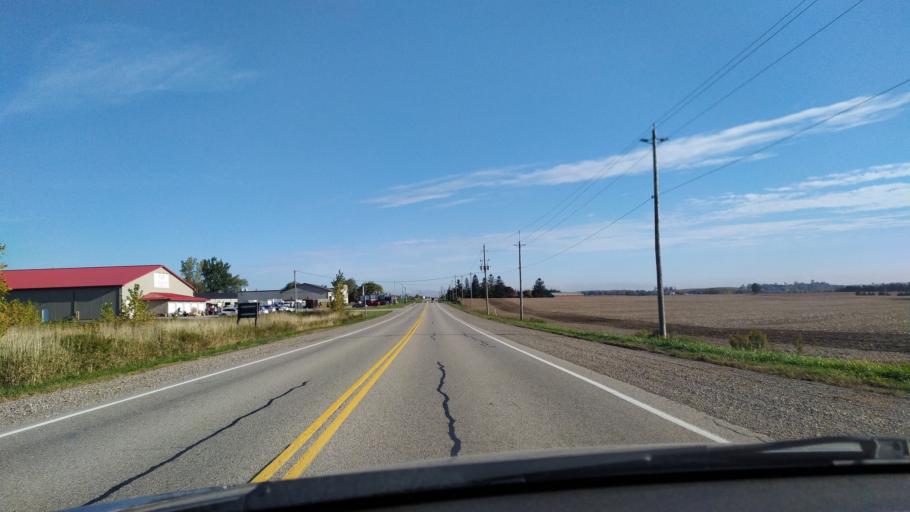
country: CA
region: Ontario
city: Stratford
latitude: 43.4796
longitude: -80.7794
